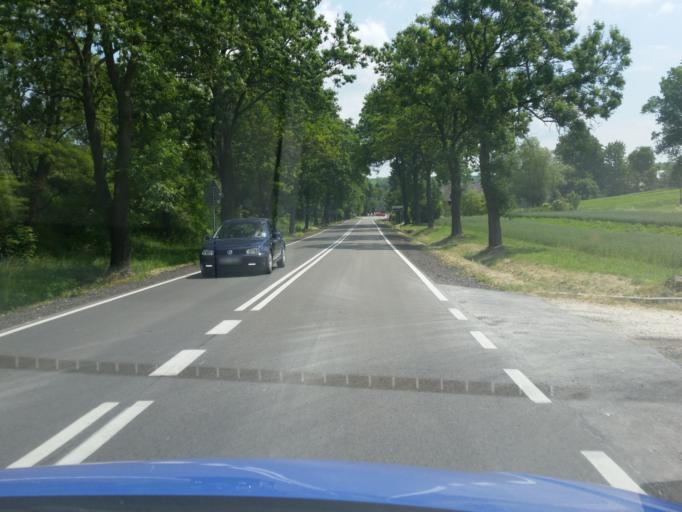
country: PL
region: Swietokrzyskie
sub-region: Powiat pinczowski
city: Dzialoszyce
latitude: 50.3259
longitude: 20.2295
